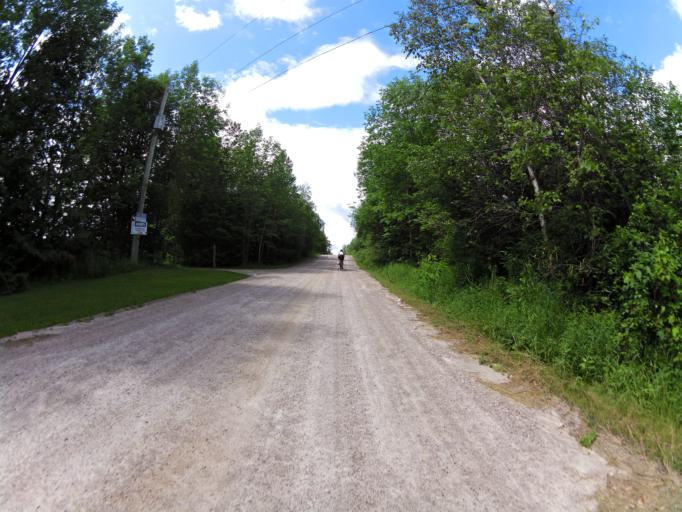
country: CA
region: Ontario
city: Perth
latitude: 45.0315
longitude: -76.5044
